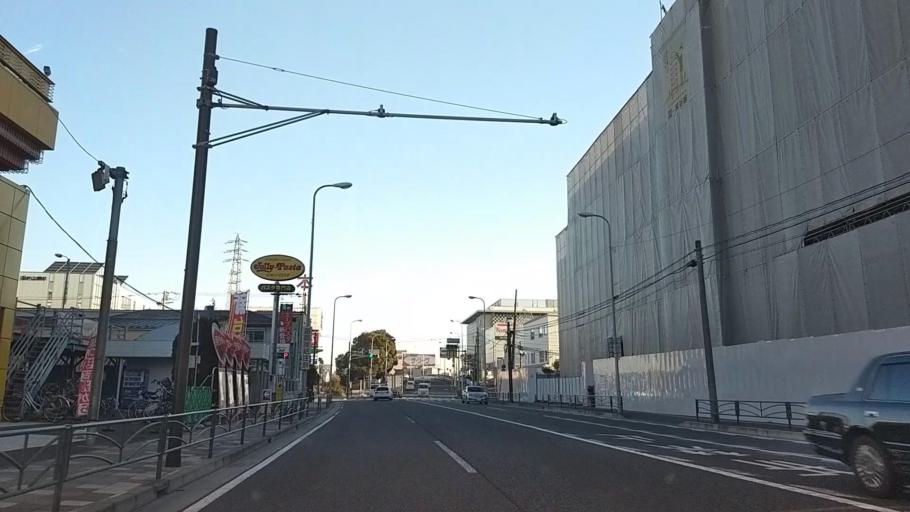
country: JP
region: Kanagawa
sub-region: Kawasaki-shi
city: Kawasaki
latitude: 35.5108
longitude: 139.6837
